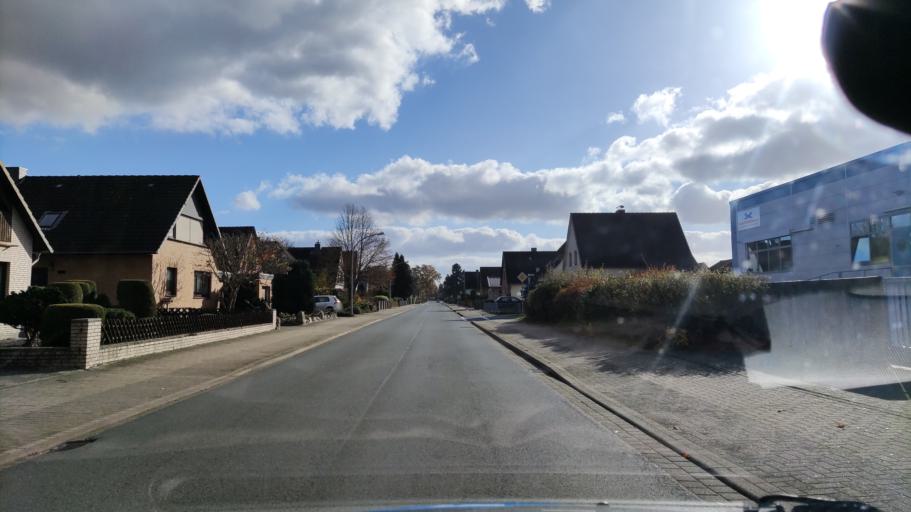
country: DE
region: Lower Saxony
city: Munster
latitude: 52.9953
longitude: 10.1044
